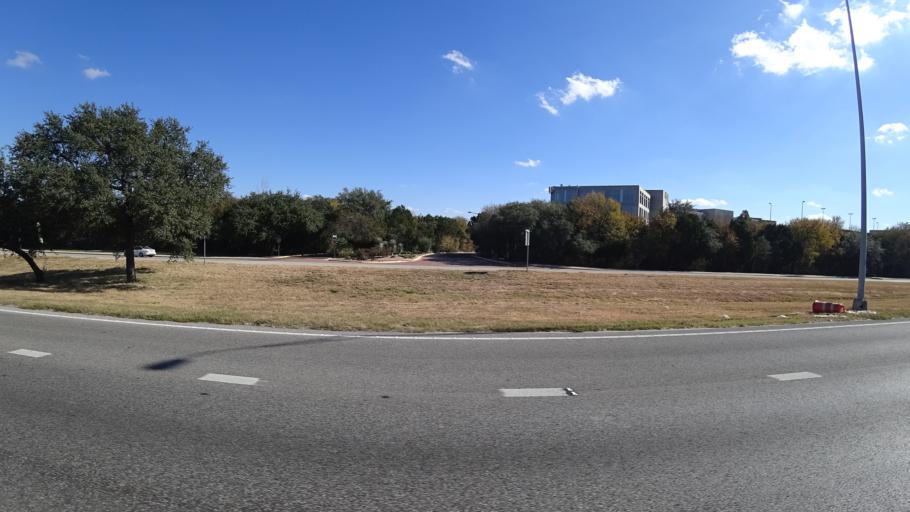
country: US
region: Texas
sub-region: Travis County
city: Rollingwood
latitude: 30.2552
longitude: -97.8011
